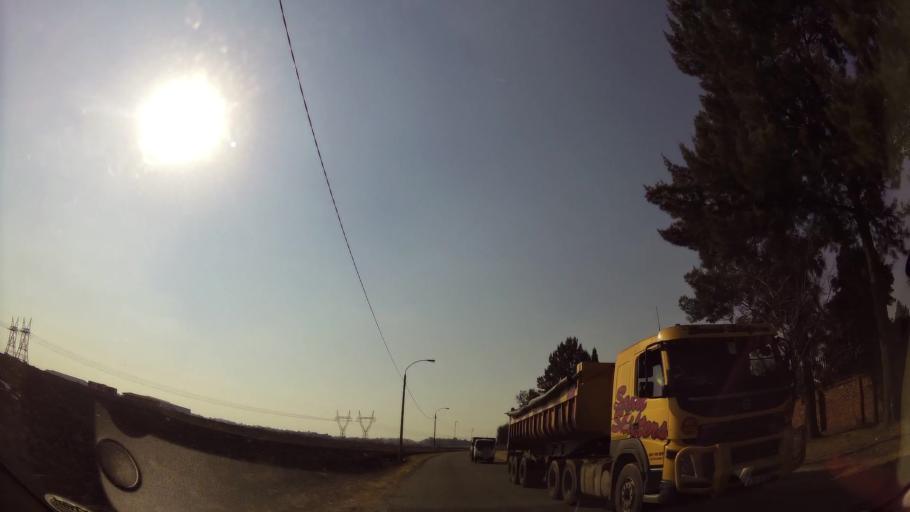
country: ZA
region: Gauteng
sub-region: Ekurhuleni Metropolitan Municipality
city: Benoni
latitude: -26.1461
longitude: 28.2813
